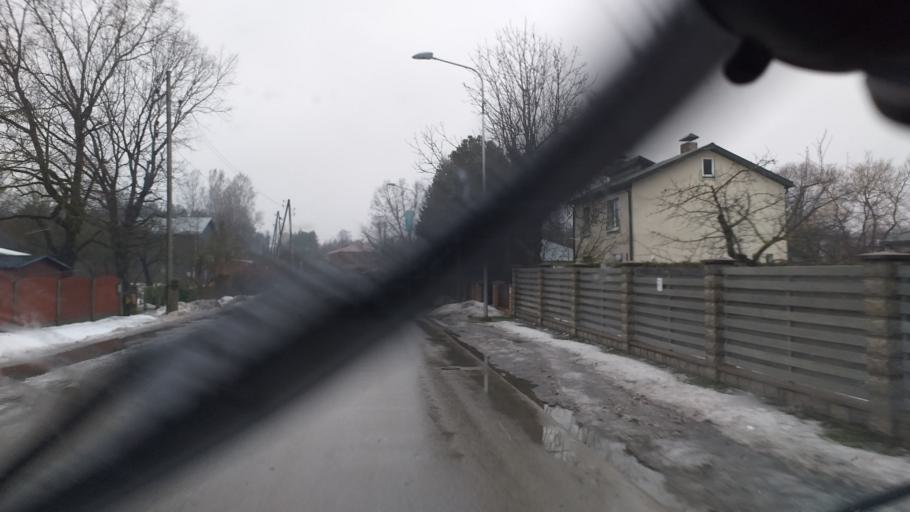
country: LV
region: Babite
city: Pinki
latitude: 56.9603
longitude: 23.9553
